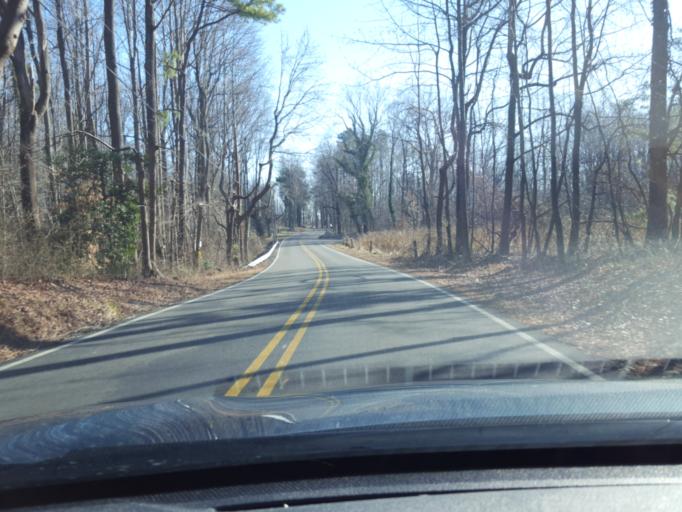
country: US
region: Maryland
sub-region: Calvert County
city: Chesapeake Beach
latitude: 38.6525
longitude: -76.5425
